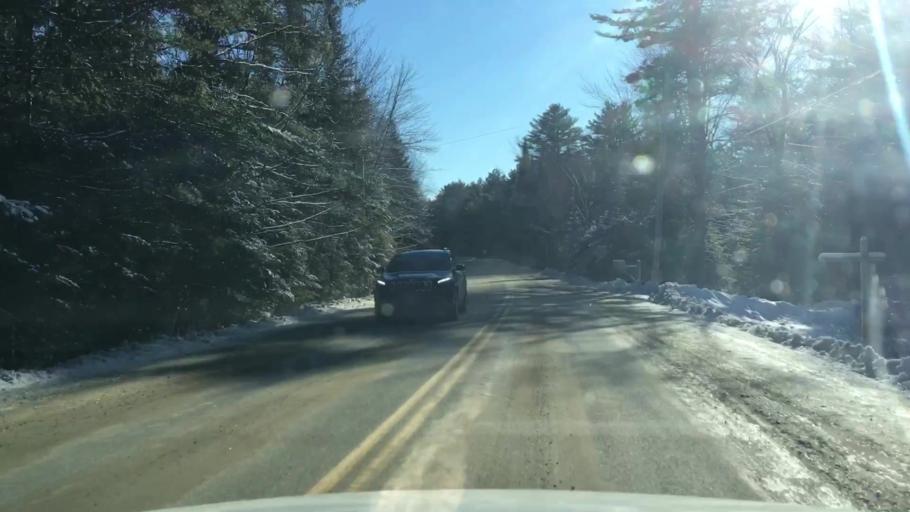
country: US
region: Maine
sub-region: Kennebec County
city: Readfield
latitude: 44.3556
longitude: -69.9915
